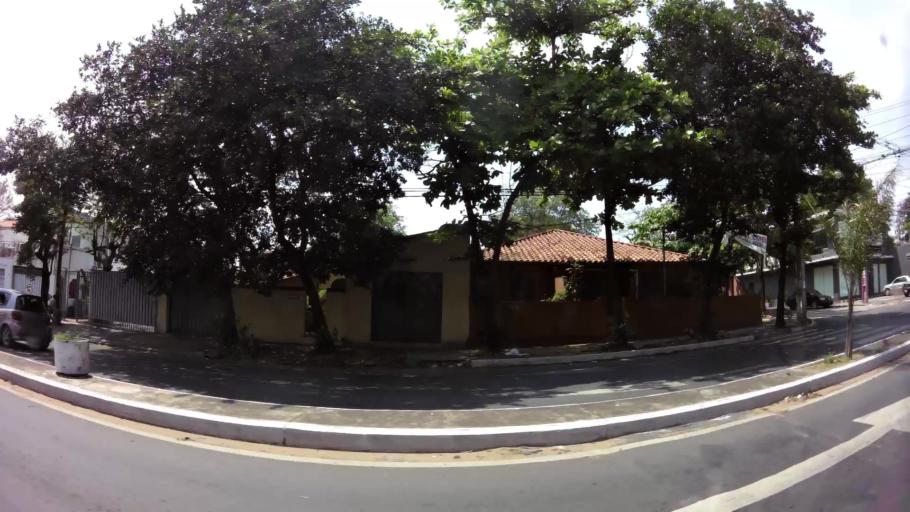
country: PY
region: Asuncion
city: Asuncion
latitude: -25.3064
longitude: -57.5955
